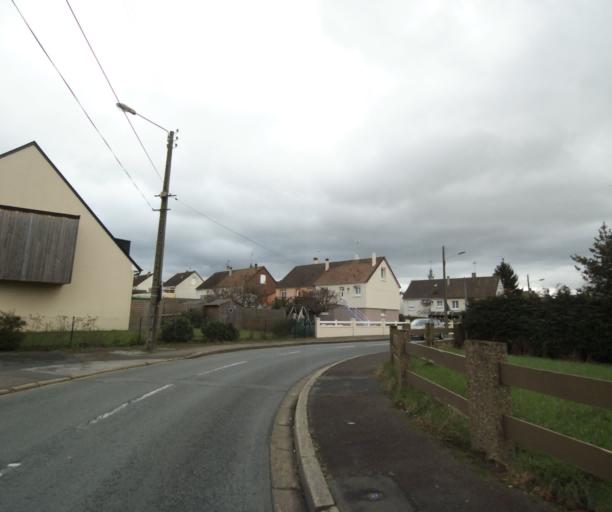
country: FR
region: Pays de la Loire
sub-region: Departement de la Sarthe
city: Le Mans
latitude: 47.9672
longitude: 0.1980
